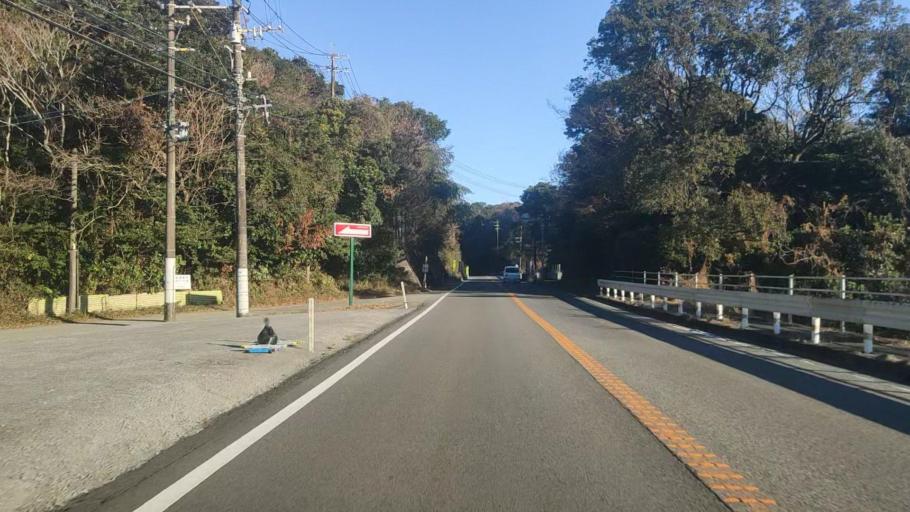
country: JP
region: Miyazaki
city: Nobeoka
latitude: 32.3494
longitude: 131.6228
